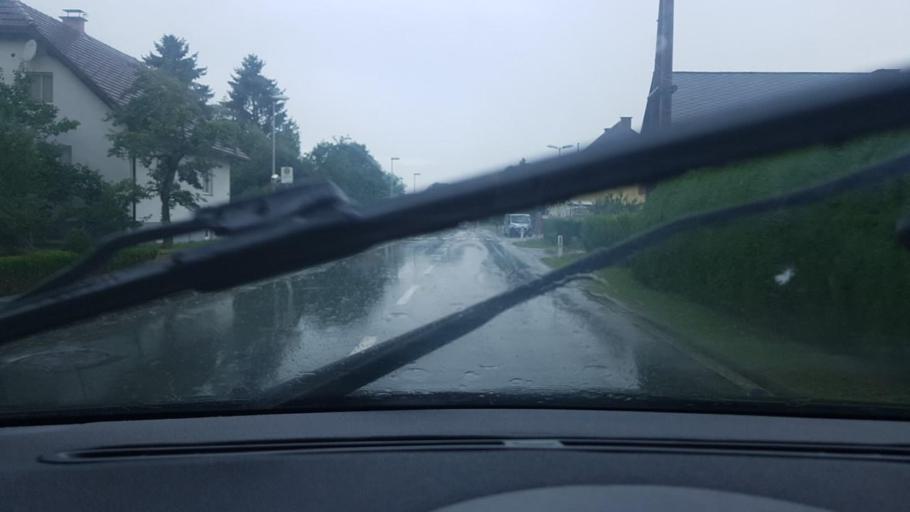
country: AT
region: Styria
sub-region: Politischer Bezirk Graz-Umgebung
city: Zettling
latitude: 46.9583
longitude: 15.4279
